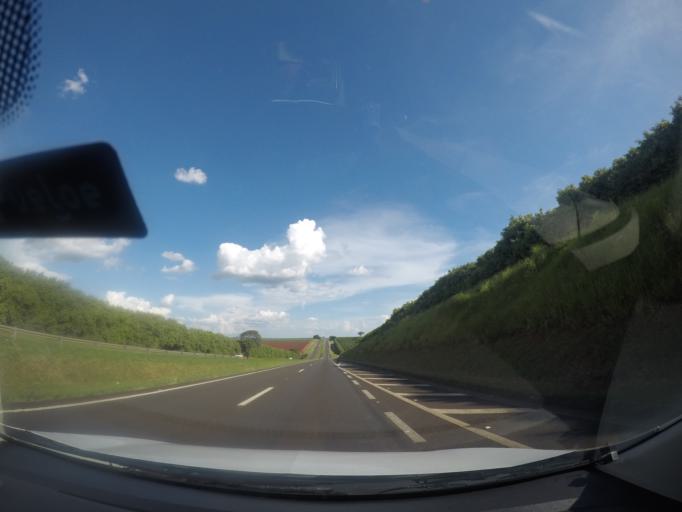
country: BR
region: Sao Paulo
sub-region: Bebedouro
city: Bebedouro
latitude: -21.0113
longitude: -48.4272
